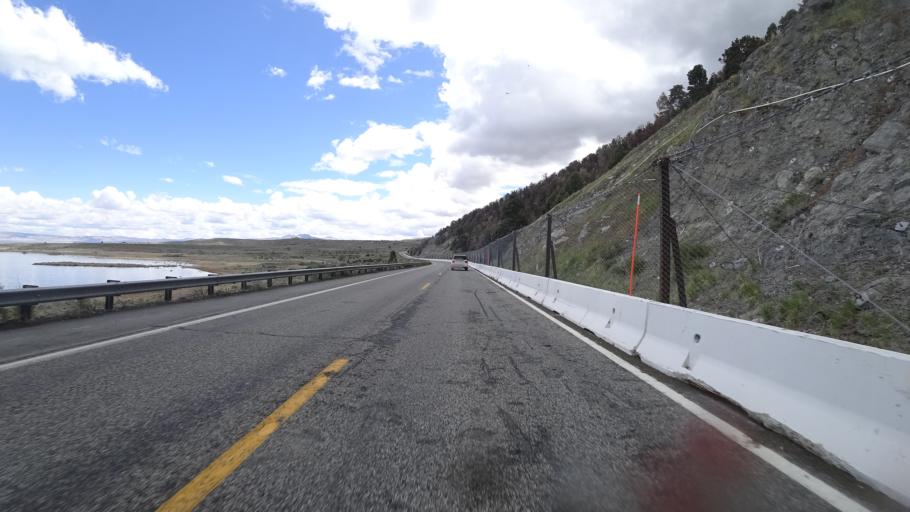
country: US
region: California
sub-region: Mono County
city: Bridgeport
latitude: 37.9809
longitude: -119.1385
